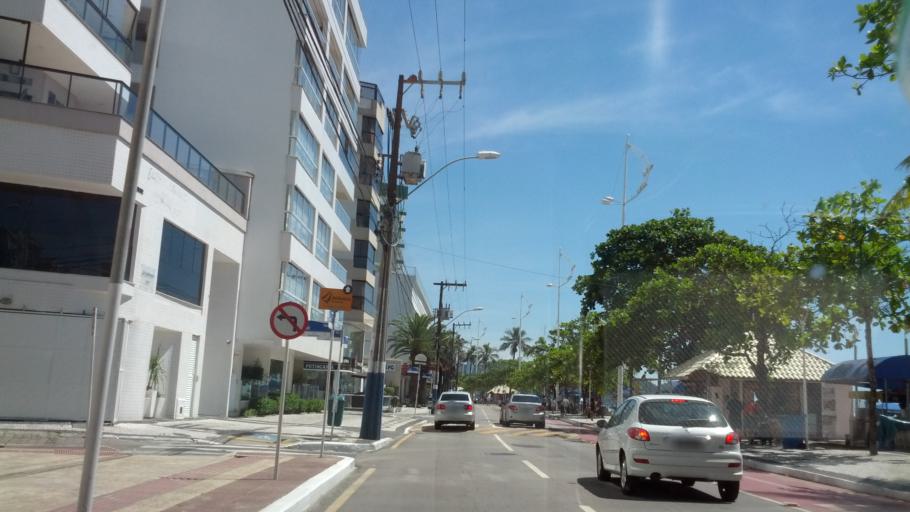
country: BR
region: Santa Catarina
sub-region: Balneario Camboriu
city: Balneario Camboriu
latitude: -26.9923
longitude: -48.6288
